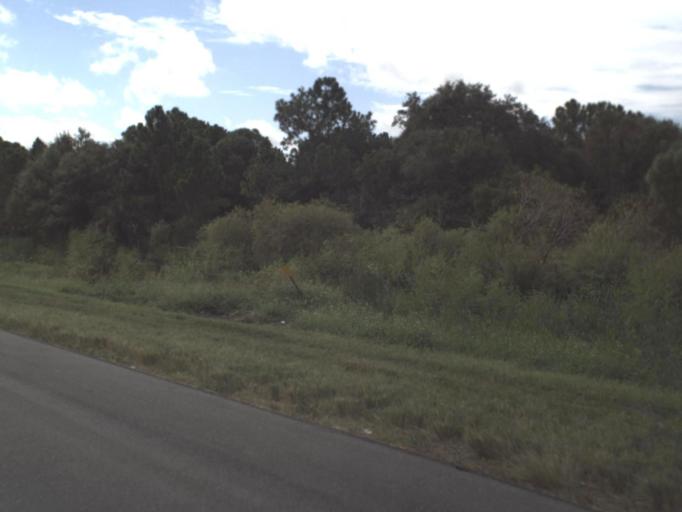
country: US
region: Florida
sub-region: Sarasota County
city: Warm Mineral Springs
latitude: 27.1077
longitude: -82.3062
